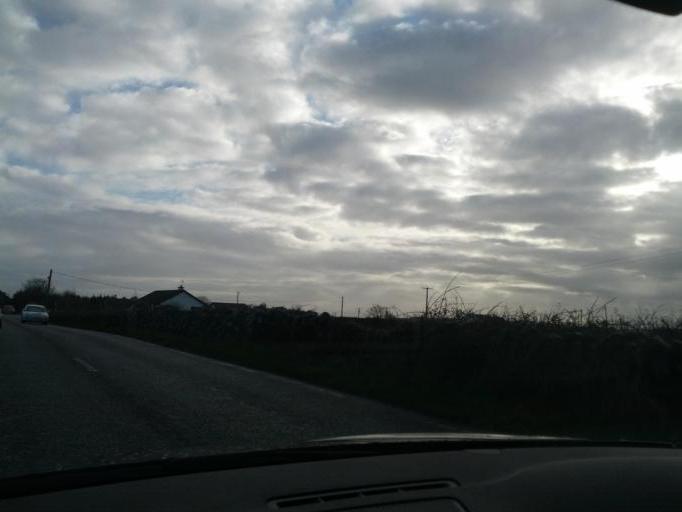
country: IE
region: Connaught
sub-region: County Galway
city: Oranmore
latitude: 53.3090
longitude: -8.8995
